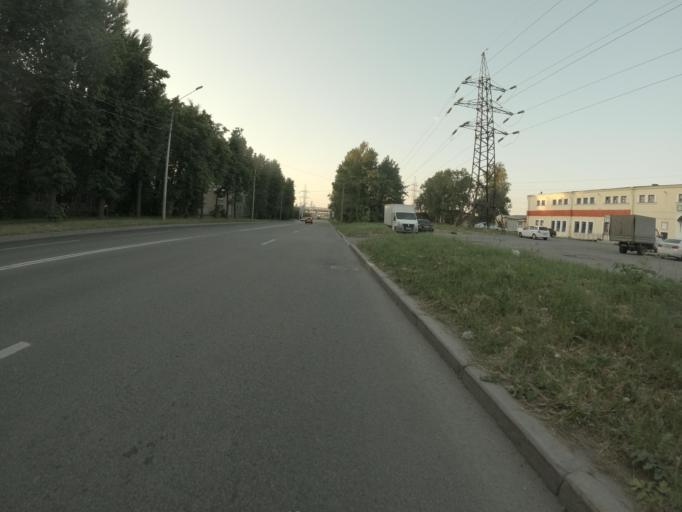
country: RU
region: St.-Petersburg
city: Avtovo
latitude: 59.8772
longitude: 30.2783
